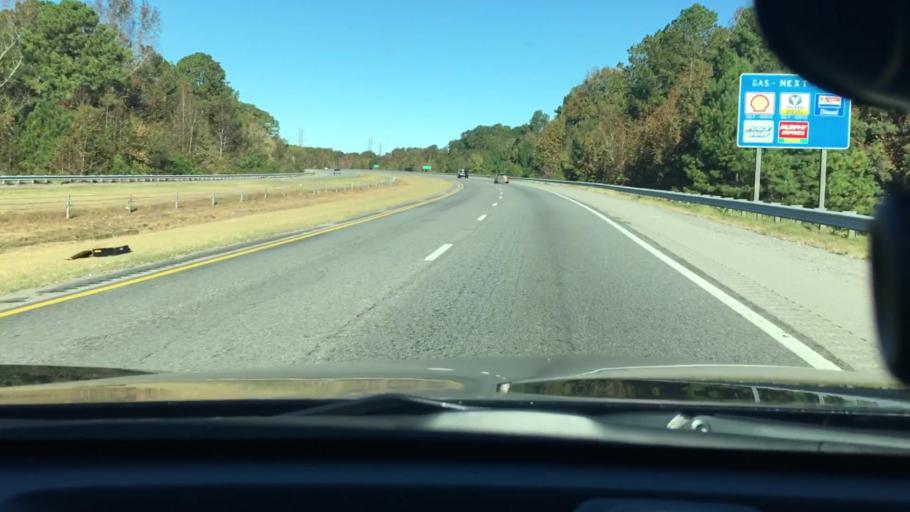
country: US
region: North Carolina
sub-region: Edgecombe County
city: Princeville
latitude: 35.8821
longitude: -77.5303
